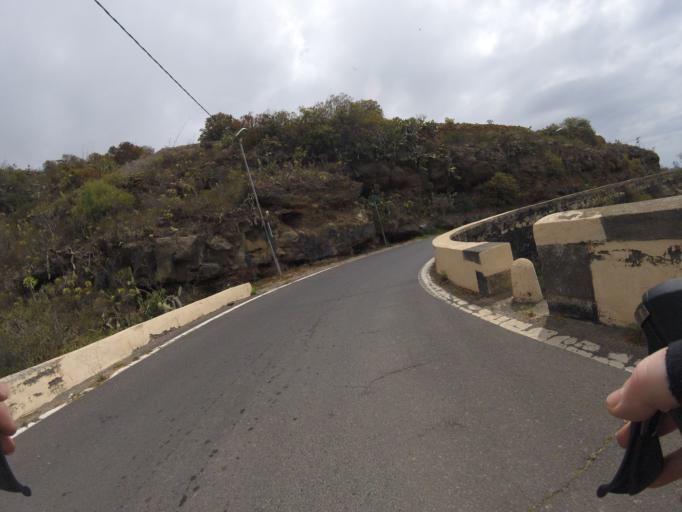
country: ES
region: Canary Islands
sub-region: Provincia de Santa Cruz de Tenerife
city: Guimar
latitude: 28.2755
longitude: -16.4141
